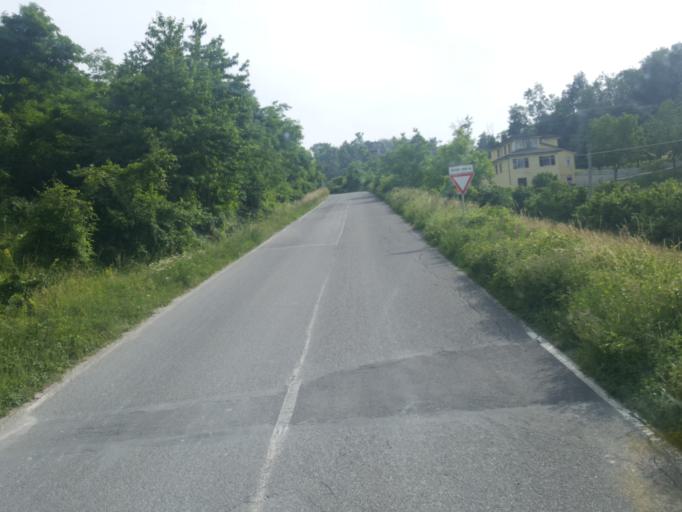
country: IT
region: Emilia-Romagna
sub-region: Provincia di Piacenza
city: Ponte dell'Olio
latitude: 44.8766
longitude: 9.6257
